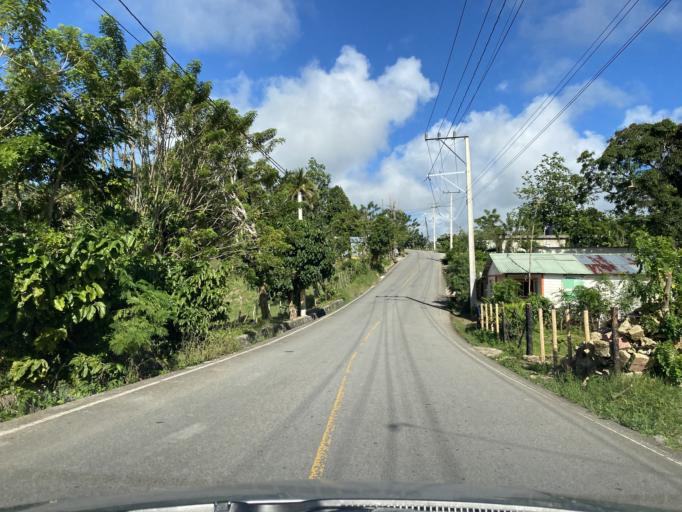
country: DO
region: Samana
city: Sanchez
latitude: 19.2553
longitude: -69.5722
